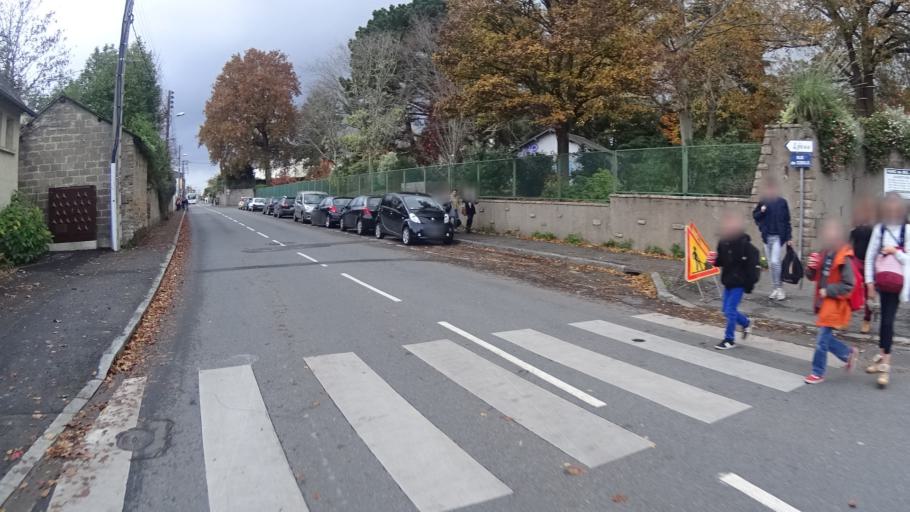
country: FR
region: Brittany
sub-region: Departement d'Ille-et-Vilaine
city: Redon
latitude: 47.6529
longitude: -2.0888
